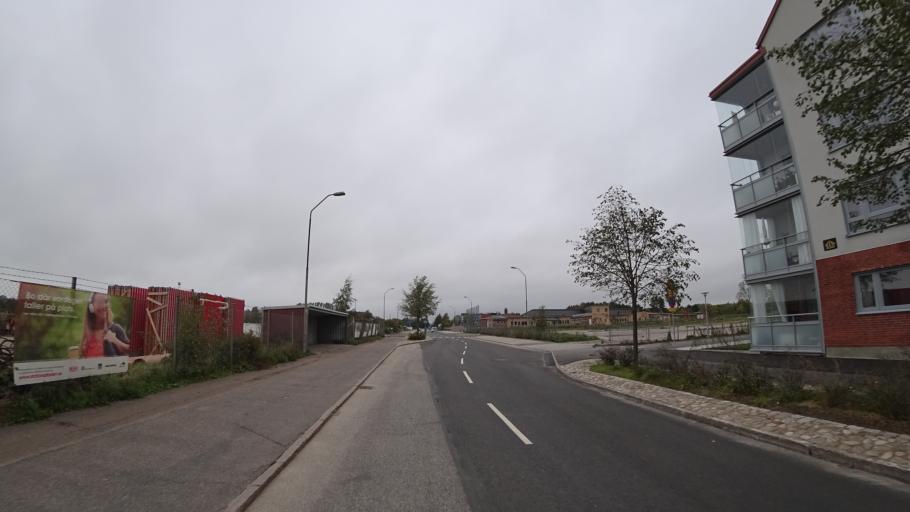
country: SE
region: Skane
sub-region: Kavlinge Kommun
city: Kaevlinge
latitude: 55.7942
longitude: 13.1182
